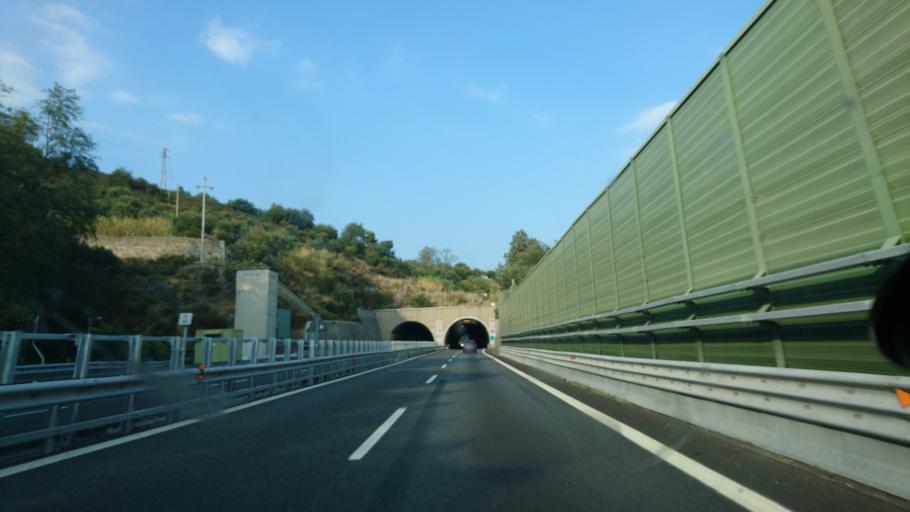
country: IT
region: Liguria
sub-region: Provincia di Savona
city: Savona
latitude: 44.3125
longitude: 8.4681
